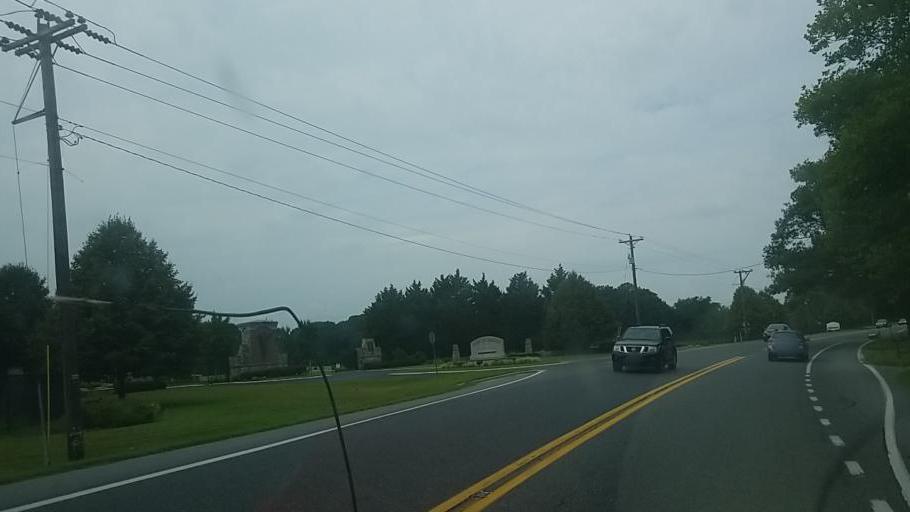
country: US
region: Delaware
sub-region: Sussex County
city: Long Neck
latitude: 38.5538
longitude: -75.1929
